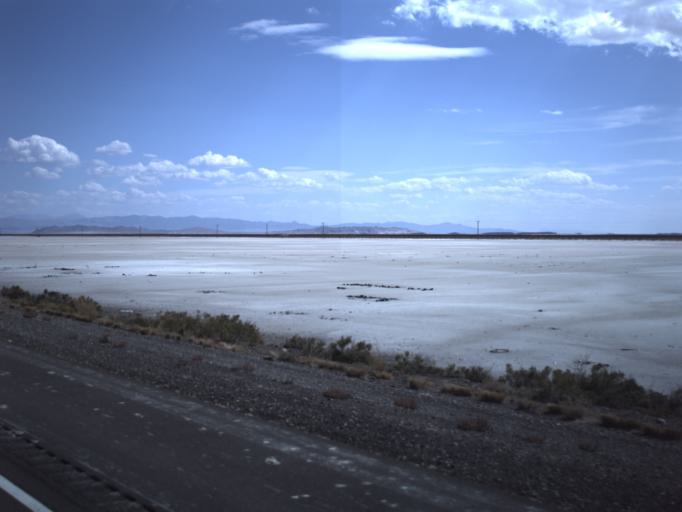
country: US
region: Utah
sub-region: Tooele County
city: Wendover
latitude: 40.7300
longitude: -113.4611
